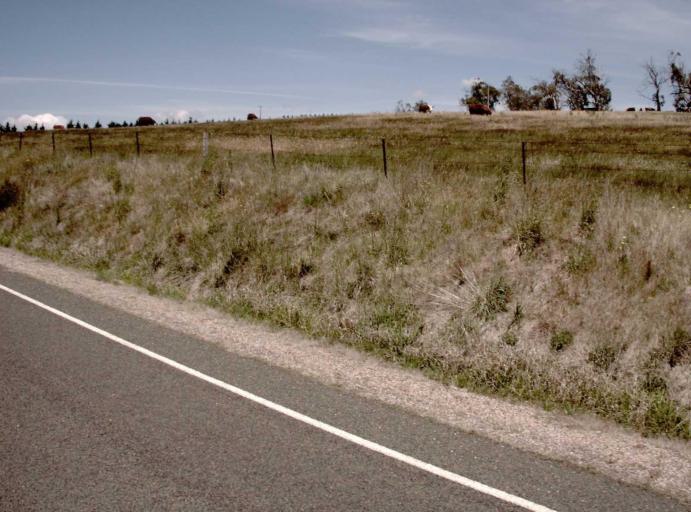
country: AU
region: Victoria
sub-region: Alpine
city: Mount Beauty
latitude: -37.1347
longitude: 147.6456
